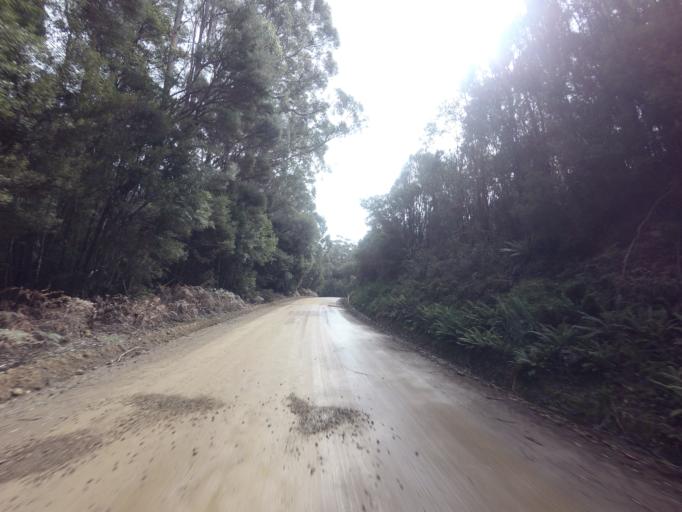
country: AU
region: Tasmania
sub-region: Huon Valley
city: Geeveston
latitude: -43.4071
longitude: 146.8688
